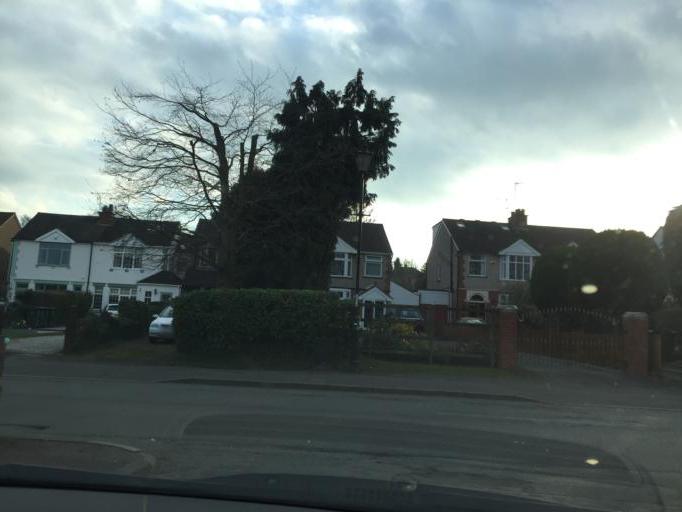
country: GB
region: England
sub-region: Coventry
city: Keresley
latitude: 52.4302
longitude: -1.5670
